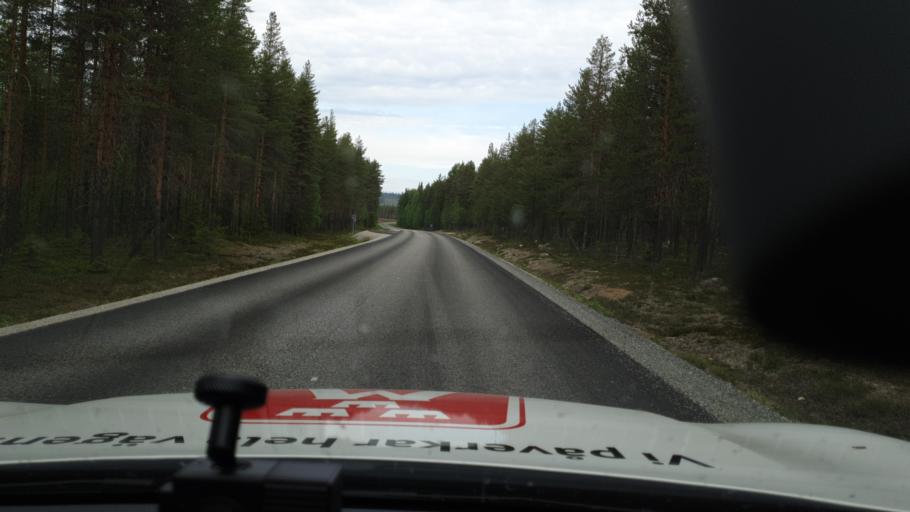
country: SE
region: Vaesterbotten
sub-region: Mala Kommun
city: Mala
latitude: 64.9478
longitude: 18.6130
